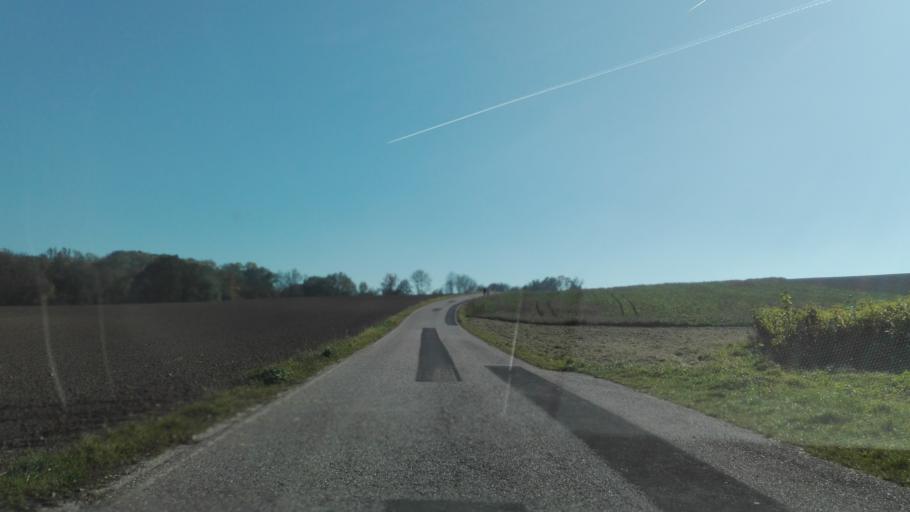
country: AT
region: Upper Austria
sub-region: Politischer Bezirk Urfahr-Umgebung
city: Ottensheim
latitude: 48.2909
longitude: 14.1599
